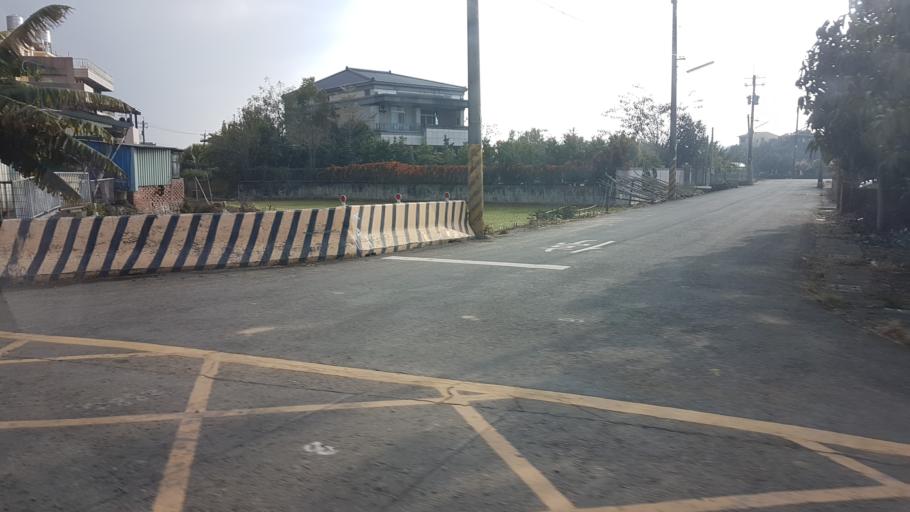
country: TW
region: Taiwan
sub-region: Chiayi
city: Jiayi Shi
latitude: 23.3898
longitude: 120.4340
